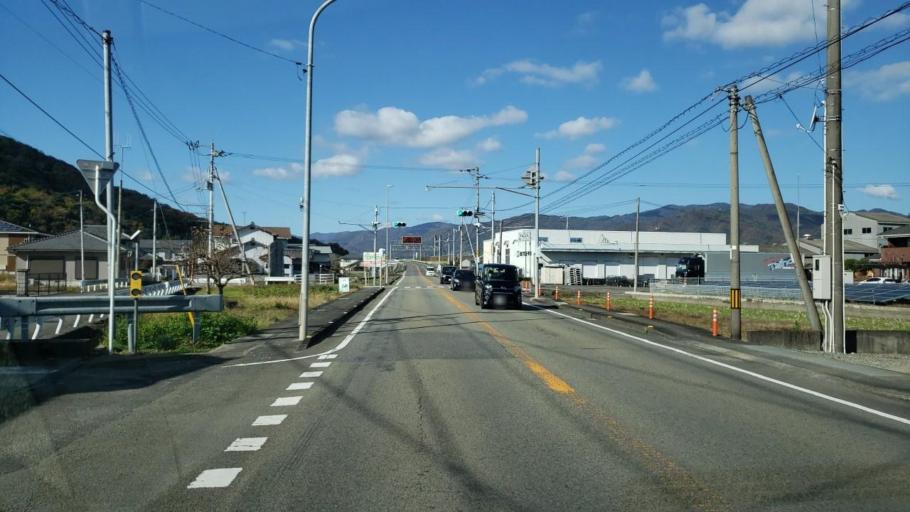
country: JP
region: Tokushima
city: Wakimachi
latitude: 34.0615
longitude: 134.2071
